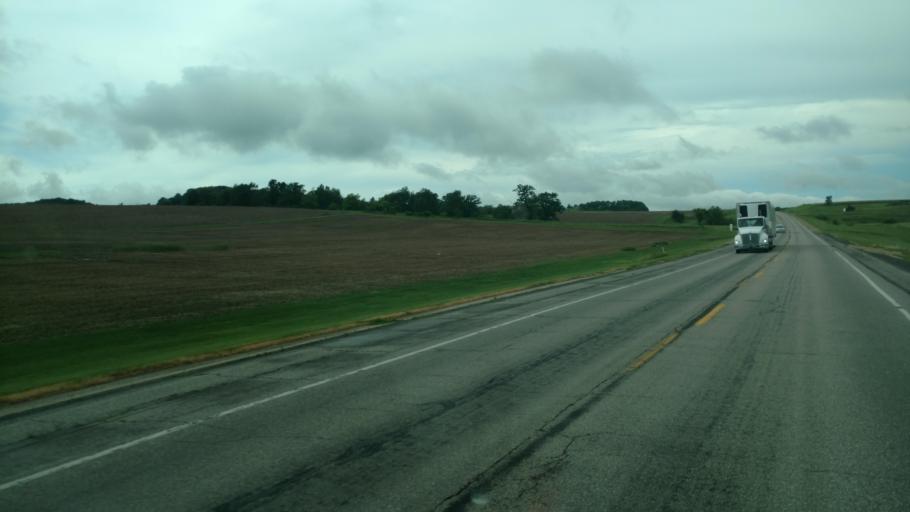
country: US
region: Wisconsin
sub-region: Vernon County
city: Hillsboro
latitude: 43.6353
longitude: -90.3573
